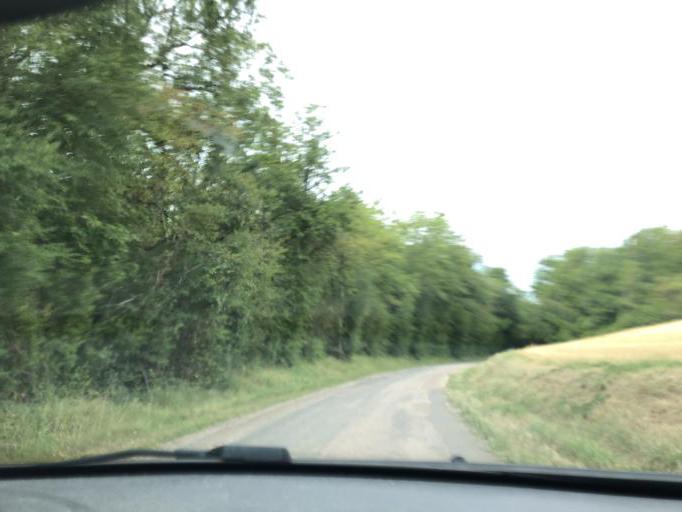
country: FR
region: Bourgogne
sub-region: Departement de l'Yonne
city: Chablis
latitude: 47.7781
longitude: 3.8269
